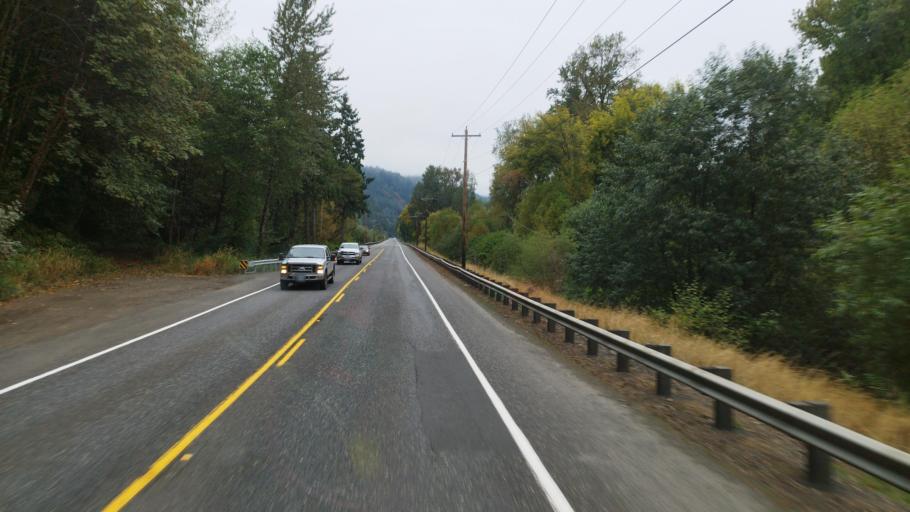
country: US
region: Washington
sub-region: Cowlitz County
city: Kalama
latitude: 46.0272
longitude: -122.8842
